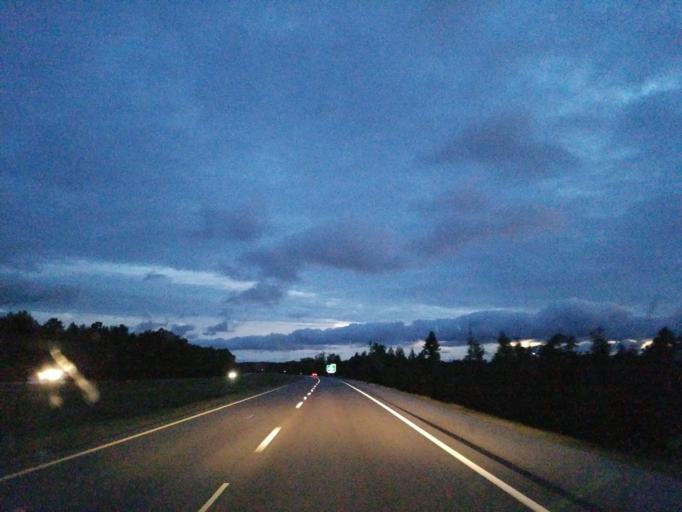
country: US
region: Mississippi
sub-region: Jones County
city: Sharon
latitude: 31.9244
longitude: -89.0030
